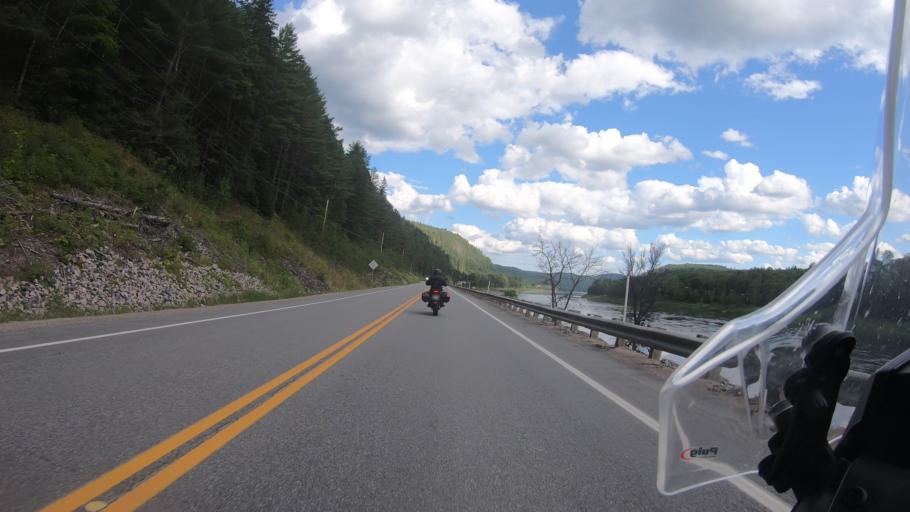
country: CA
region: Quebec
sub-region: Mauricie
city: Saint-Tite
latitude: 46.9979
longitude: -72.9225
